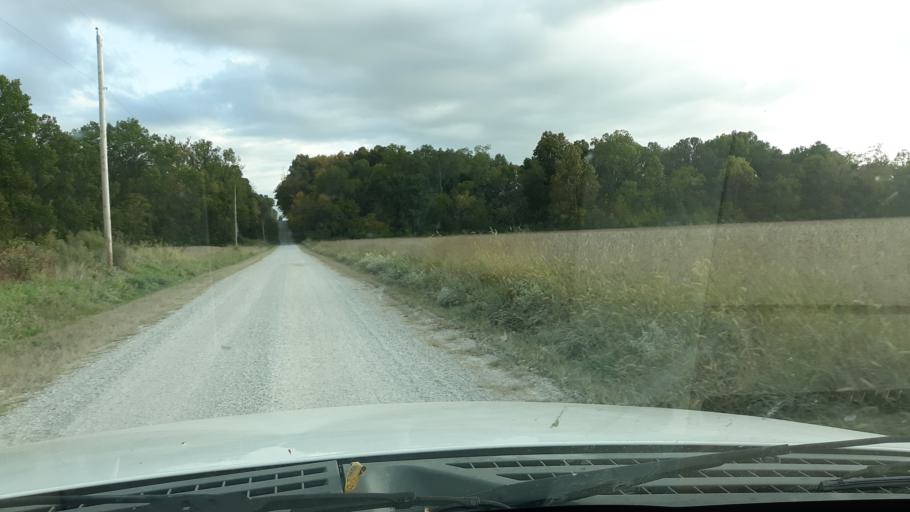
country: US
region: Illinois
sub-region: Saline County
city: Eldorado
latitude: 37.8327
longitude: -88.5026
